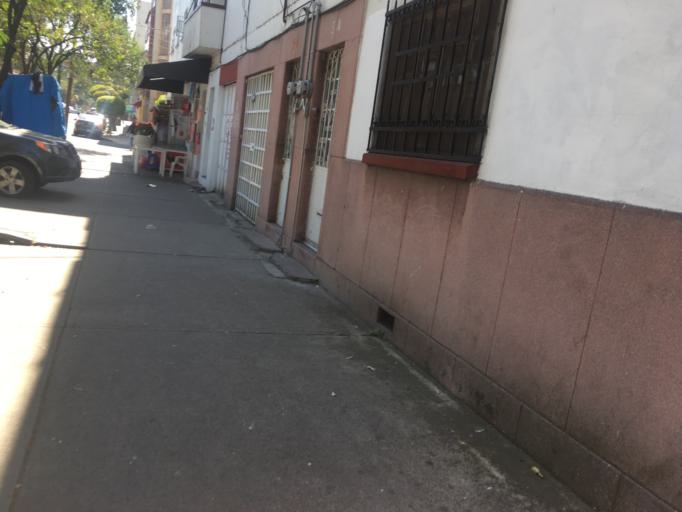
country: MX
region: Mexico City
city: Benito Juarez
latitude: 19.4073
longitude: -99.1571
